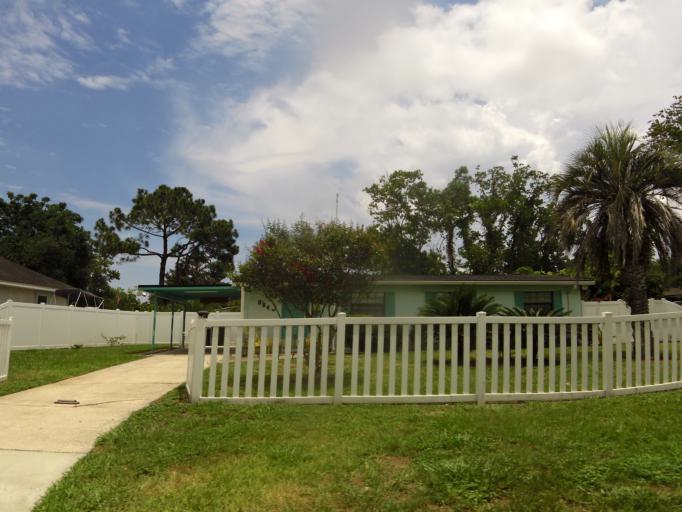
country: US
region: Florida
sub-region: Duval County
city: Atlantic Beach
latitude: 30.3334
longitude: -81.4146
